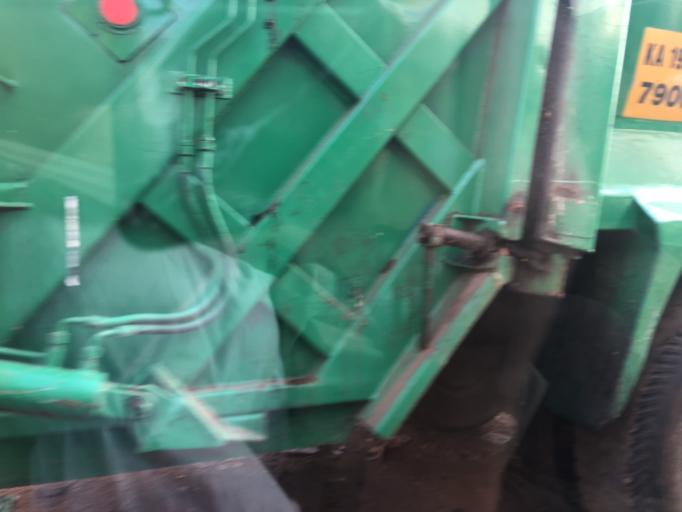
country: IN
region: Karnataka
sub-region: Dakshina Kannada
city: Mangalore
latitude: 12.8657
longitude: 74.8381
